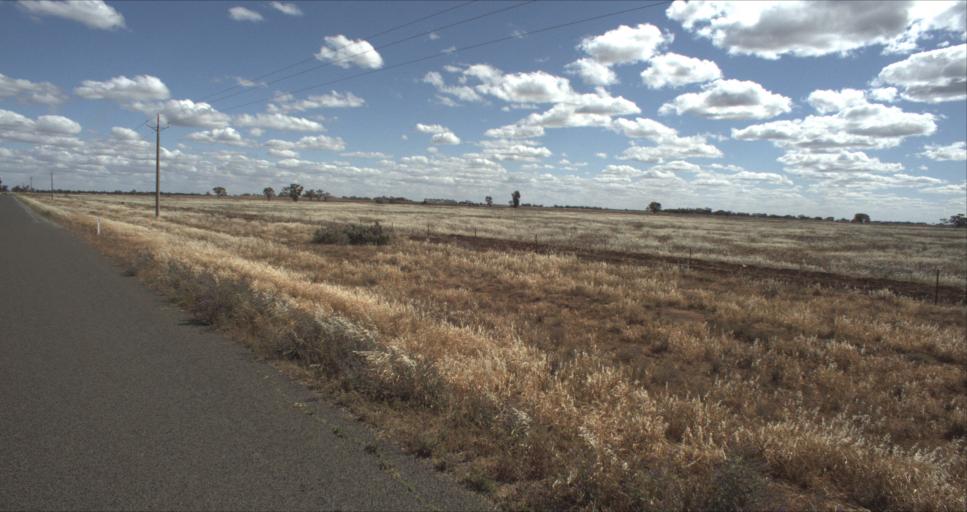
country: AU
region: New South Wales
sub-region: Leeton
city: Leeton
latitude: -34.4678
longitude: 146.2515
